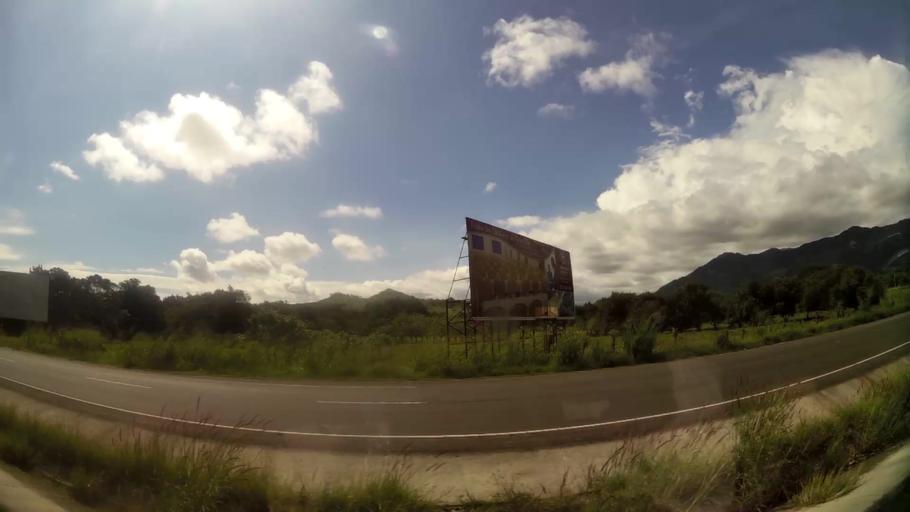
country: PA
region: Panama
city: Bejuco
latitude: 8.6250
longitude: -79.8807
